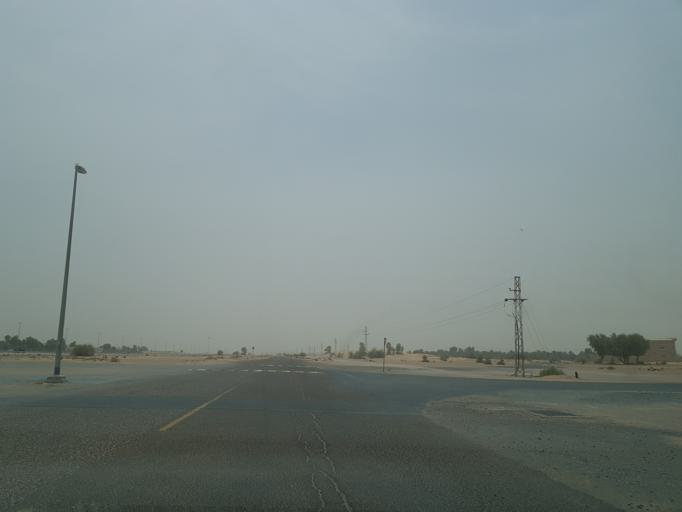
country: AE
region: Dubai
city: Dubai
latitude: 24.9307
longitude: 55.4657
